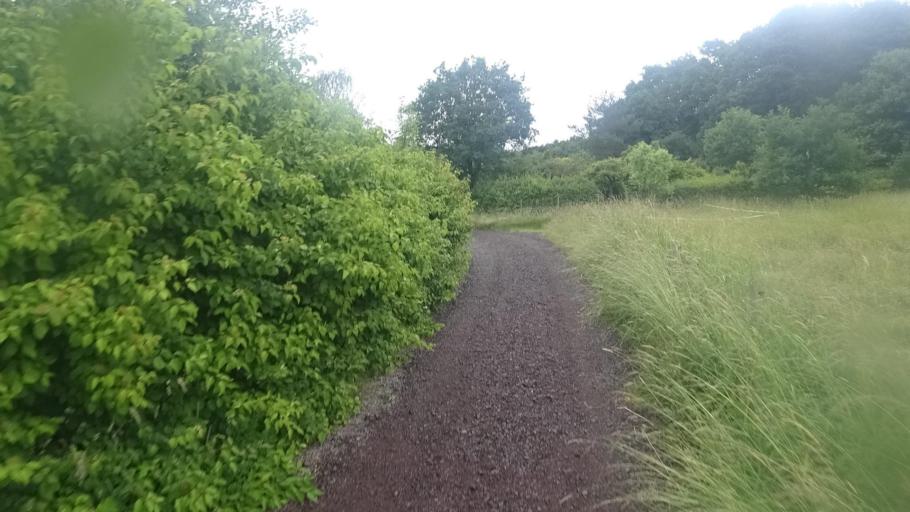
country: DE
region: Rheinland-Pfalz
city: Dernau
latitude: 50.5586
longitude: 7.0564
